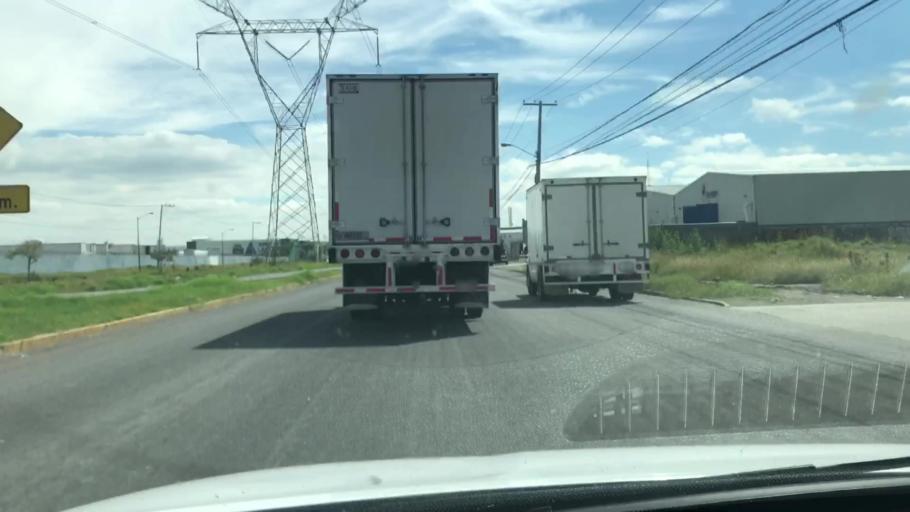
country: MX
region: Guanajuato
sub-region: Celaya
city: La Trinidad
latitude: 20.5510
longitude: -100.8077
